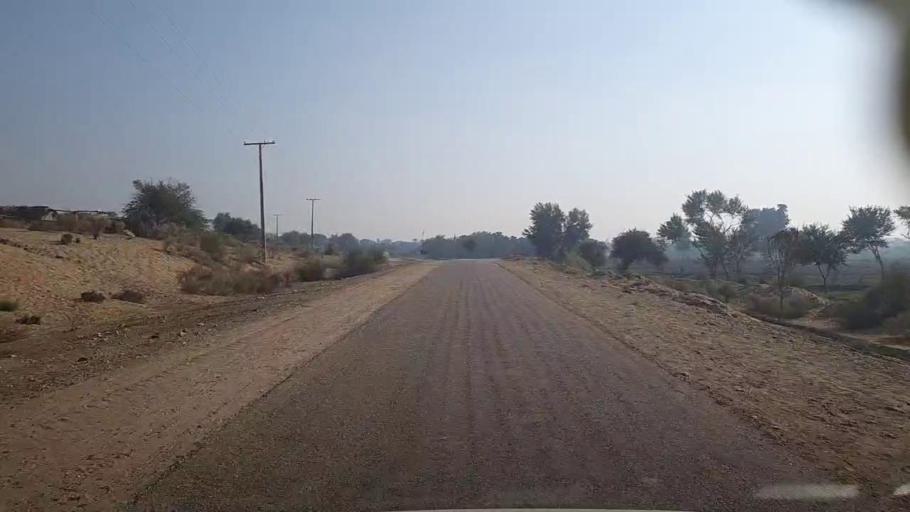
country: PK
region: Sindh
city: Kandiari
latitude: 26.8350
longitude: 68.4896
